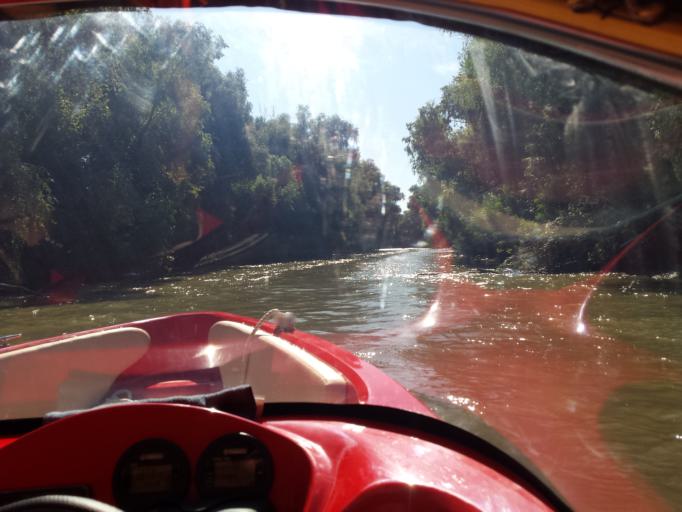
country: RO
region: Tulcea
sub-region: Comuna Pardina
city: Pardina
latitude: 45.2422
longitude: 29.0029
